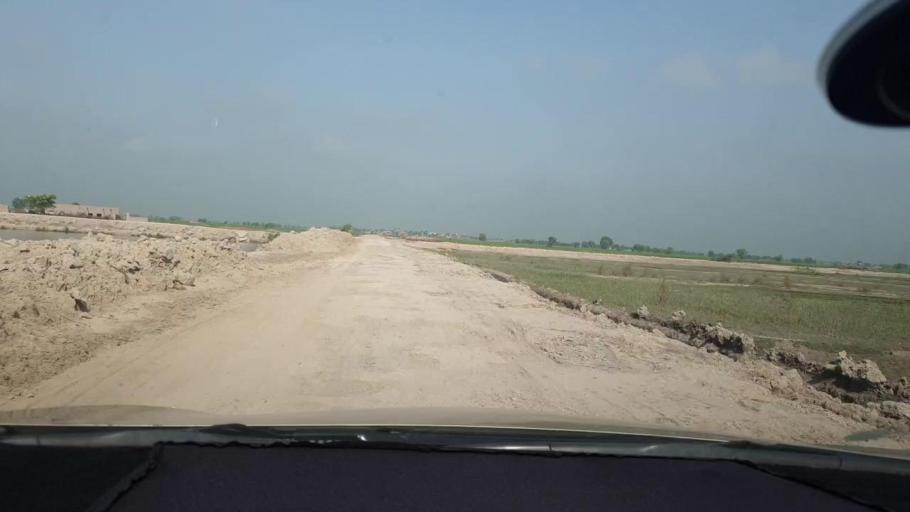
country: PK
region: Sindh
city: Kambar
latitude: 27.5366
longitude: 68.0596
